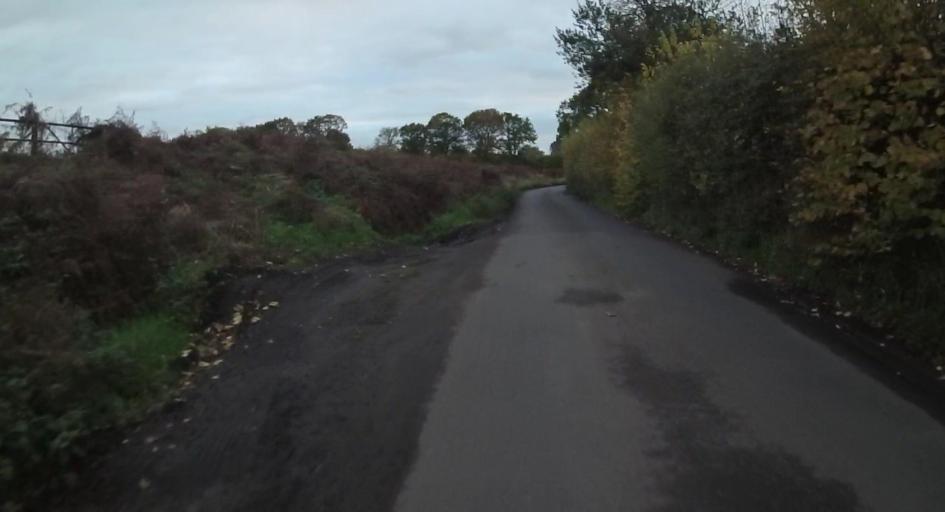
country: GB
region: England
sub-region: Hampshire
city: Lindford
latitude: 51.1245
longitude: -0.8397
